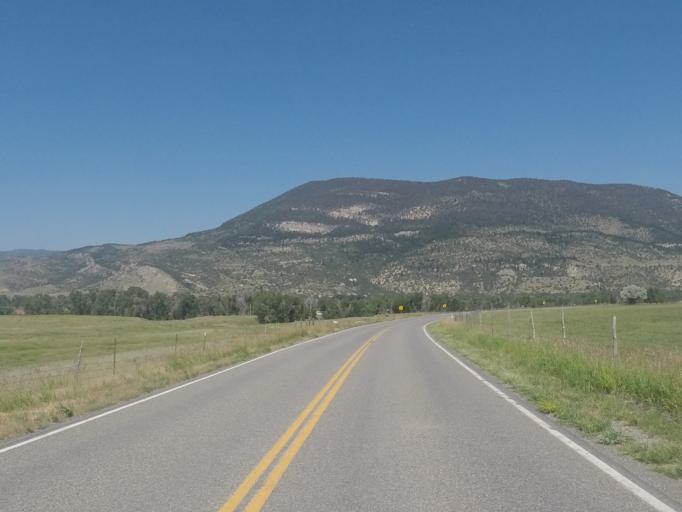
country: US
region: Montana
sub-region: Park County
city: Livingston
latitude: 45.5714
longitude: -110.5649
